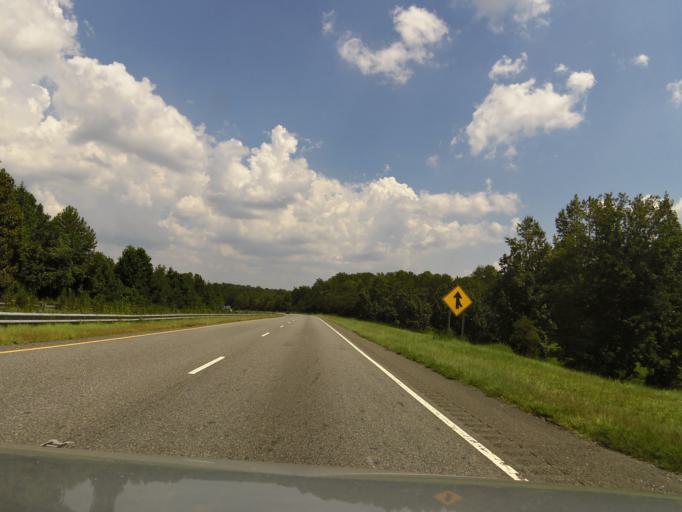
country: US
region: North Carolina
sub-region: Polk County
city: Columbus
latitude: 35.2592
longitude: -82.1824
